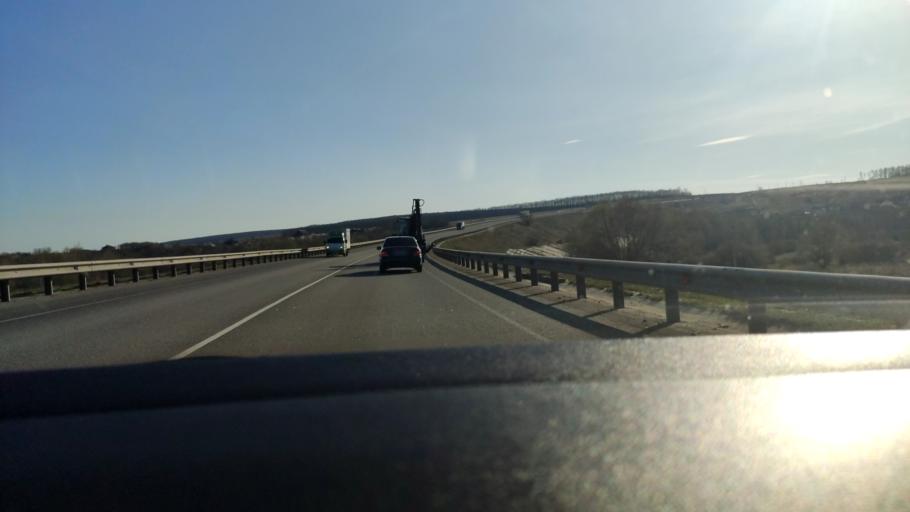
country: RU
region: Voronezj
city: Kolodeznyy
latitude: 51.3316
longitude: 39.1628
